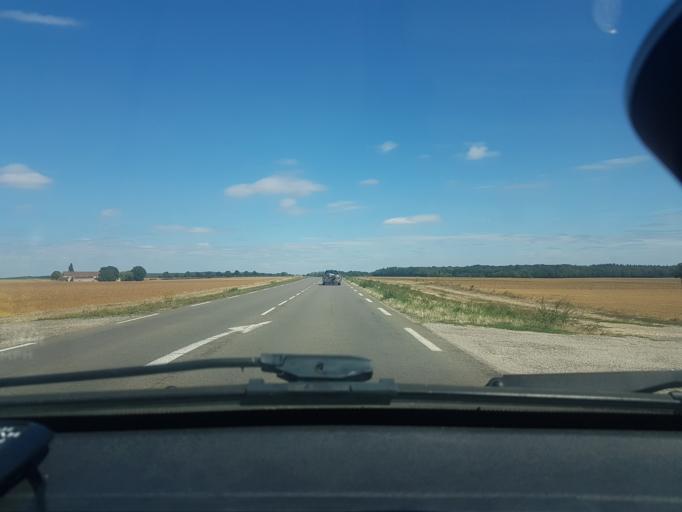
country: FR
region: Bourgogne
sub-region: Departement de la Cote-d'Or
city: Arc-sur-Tille
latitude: 47.3517
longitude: 5.2045
